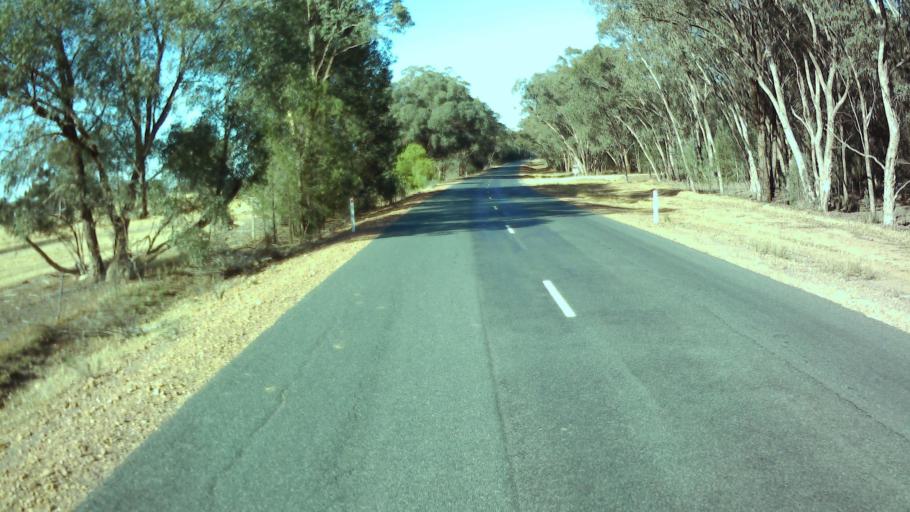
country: AU
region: New South Wales
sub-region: Weddin
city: Grenfell
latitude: -34.0104
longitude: 148.1188
